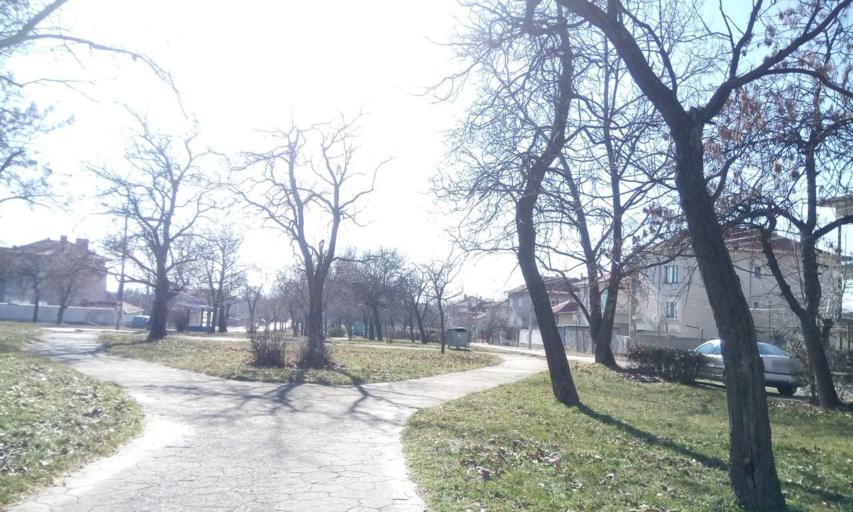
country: BG
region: Plovdiv
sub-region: Obshtina Khisarya
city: Khisarya
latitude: 42.5119
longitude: 24.7157
